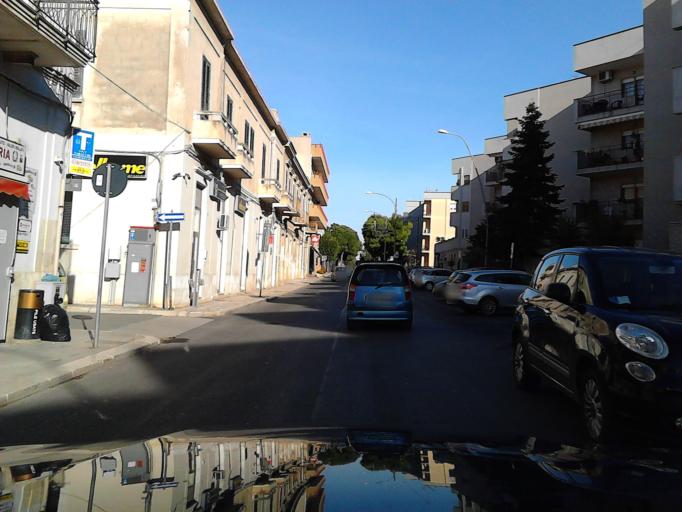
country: IT
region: Apulia
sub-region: Provincia di Bari
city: Rutigliano
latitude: 41.0114
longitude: 17.0101
